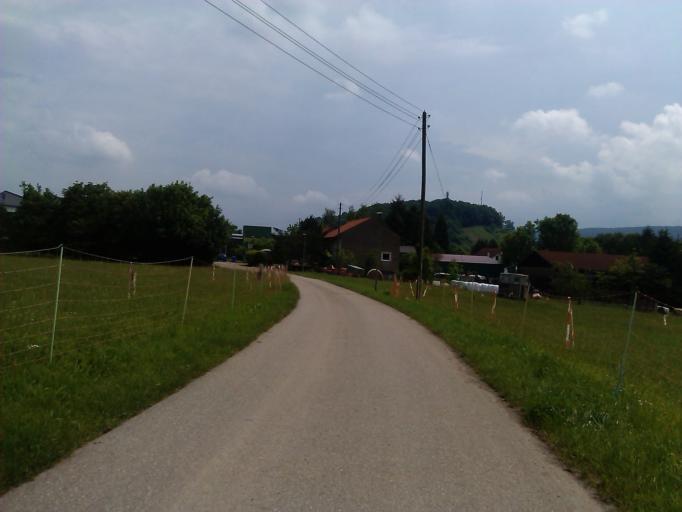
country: DE
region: Baden-Wuerttemberg
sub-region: Regierungsbezirk Stuttgart
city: Zaberfeld
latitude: 49.0627
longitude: 8.9244
